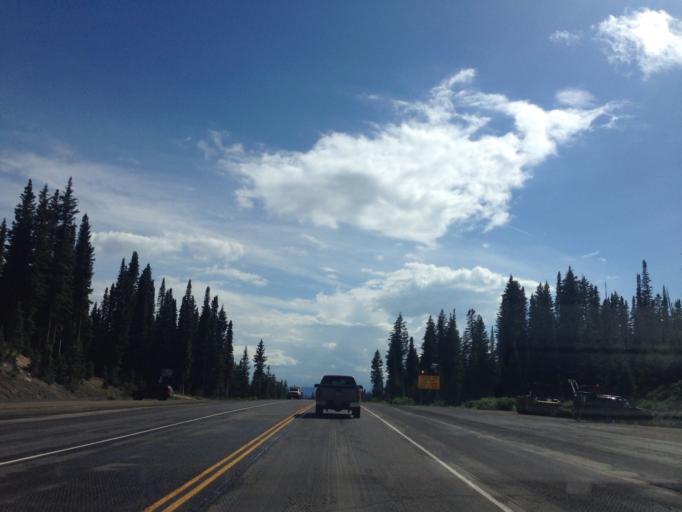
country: US
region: Colorado
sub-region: Routt County
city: Steamboat Springs
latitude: 40.3694
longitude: -106.7414
